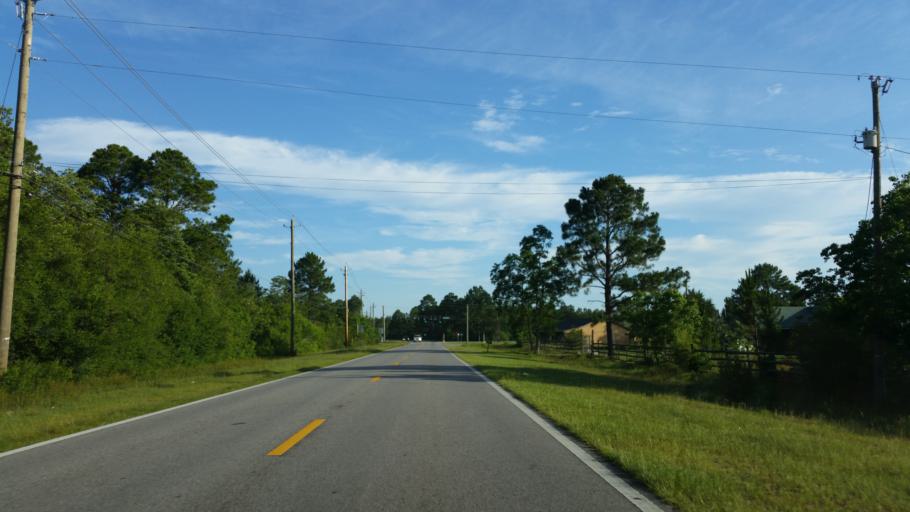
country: US
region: Florida
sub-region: Escambia County
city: Myrtle Grove
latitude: 30.3790
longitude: -87.3501
